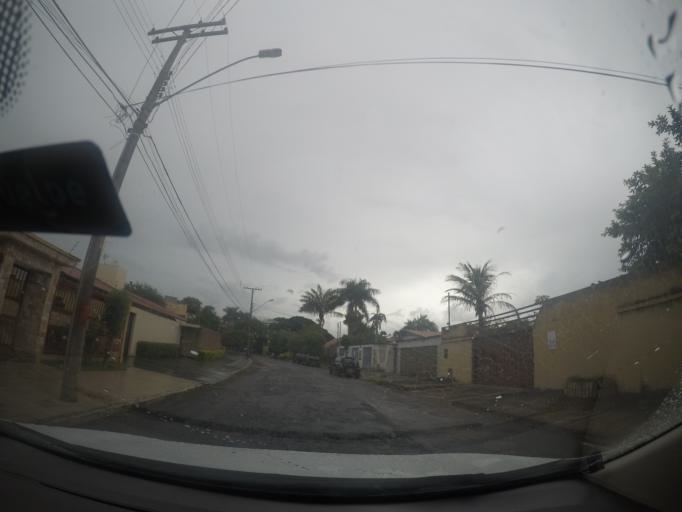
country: BR
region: Goias
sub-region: Goiania
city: Goiania
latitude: -16.6515
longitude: -49.2335
